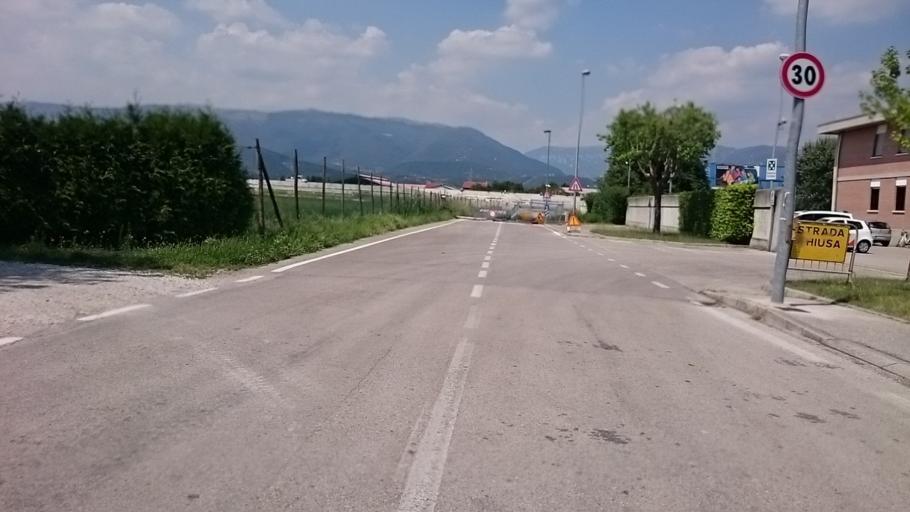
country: IT
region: Veneto
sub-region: Provincia di Vicenza
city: Bassano del Grappa
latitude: 45.7375
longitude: 11.7247
